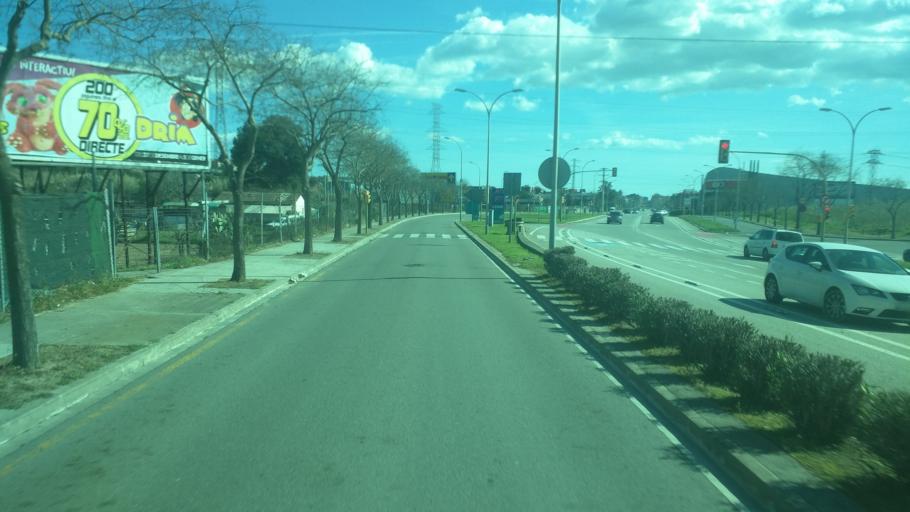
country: ES
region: Catalonia
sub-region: Provincia de Barcelona
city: Sant Feliu de Llobregat
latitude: 41.3977
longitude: 2.0334
